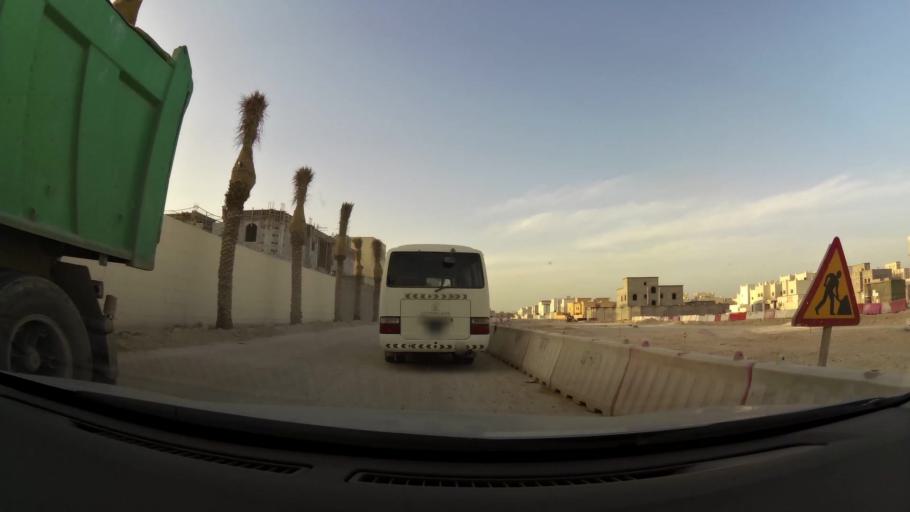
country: QA
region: Al Wakrah
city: Al Wakrah
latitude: 25.1452
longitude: 51.5952
